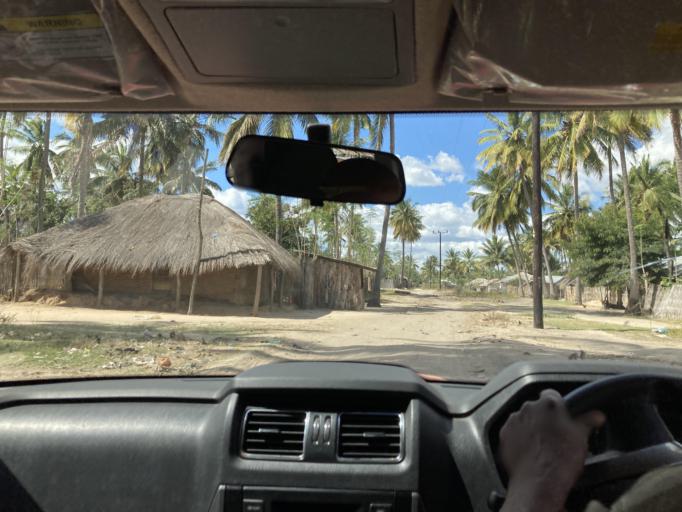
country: MZ
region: Cabo Delgado
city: Montepuez
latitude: -13.1319
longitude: 39.0149
